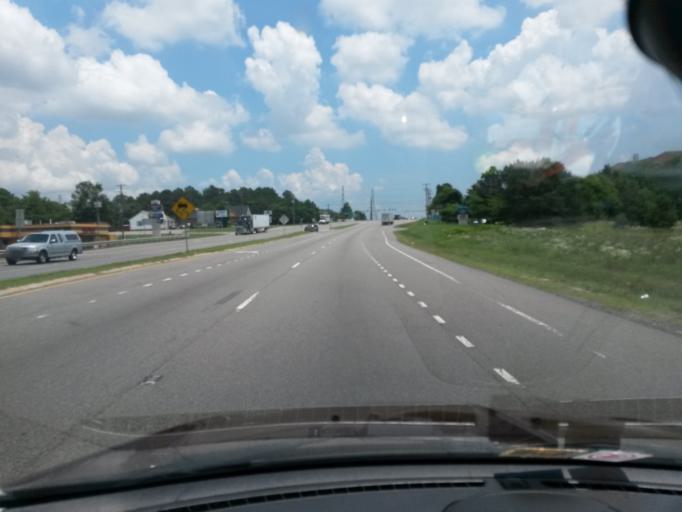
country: US
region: Virginia
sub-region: Chesterfield County
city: Chester
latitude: 37.3543
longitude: -77.4008
